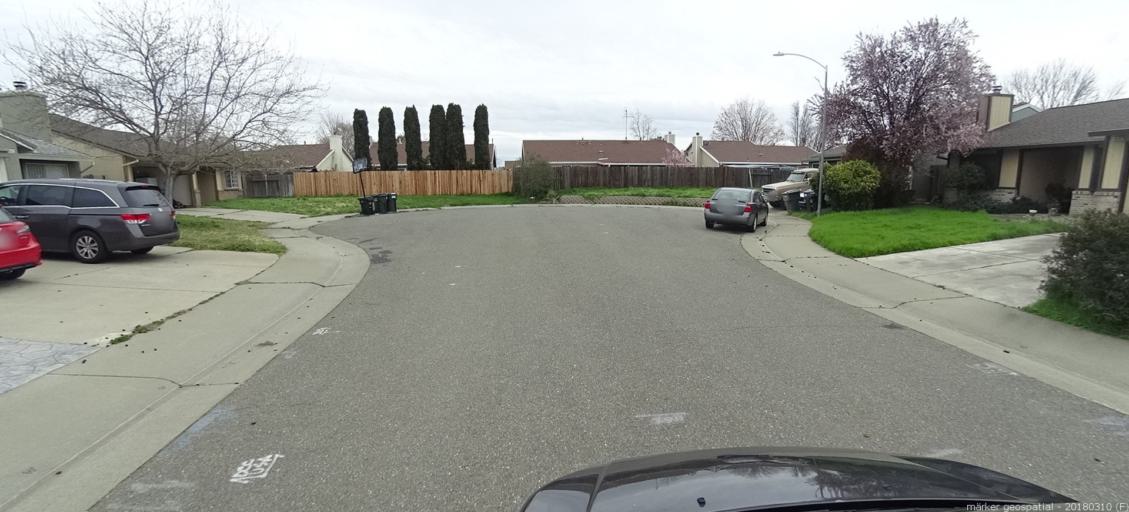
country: US
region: California
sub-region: Sacramento County
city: Florin
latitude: 38.4804
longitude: -121.3828
